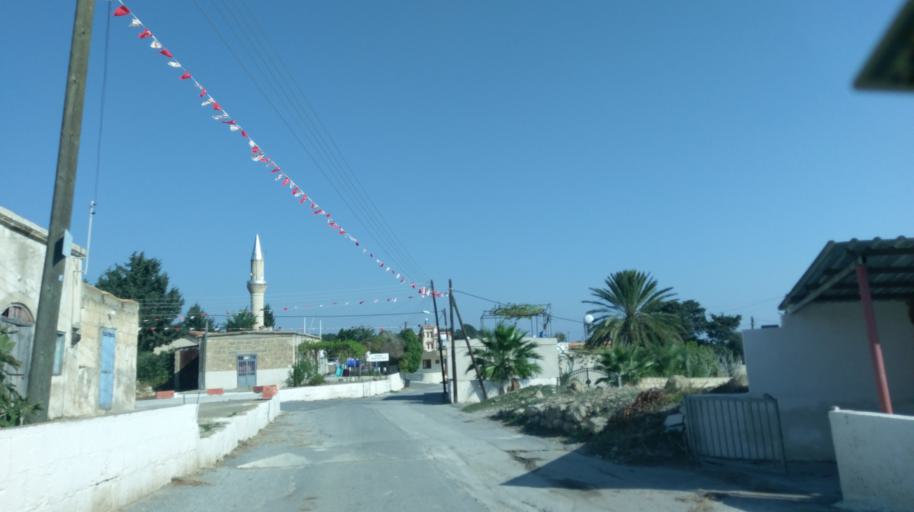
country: CY
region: Ammochostos
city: Leonarisso
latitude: 35.4904
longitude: 34.2180
